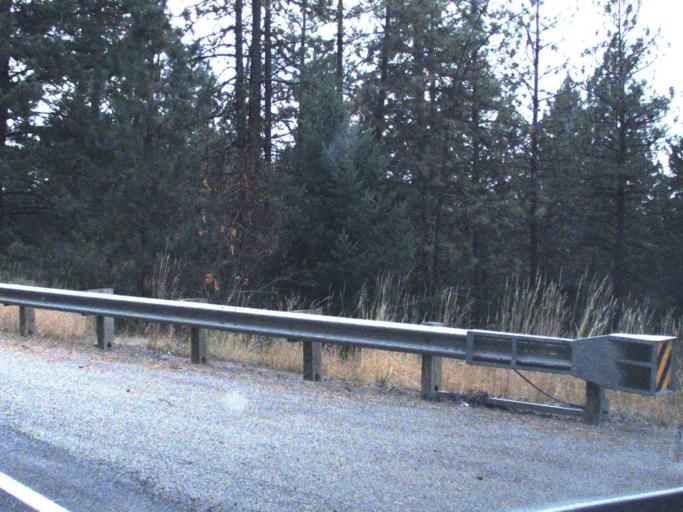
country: US
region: Washington
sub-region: Lincoln County
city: Davenport
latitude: 48.1403
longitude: -118.1913
